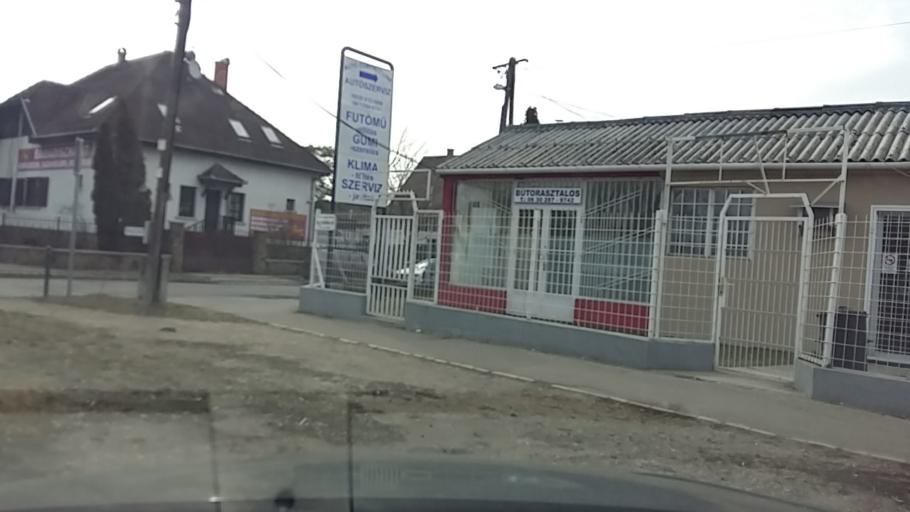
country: HU
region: Pest
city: Gyal
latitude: 47.4032
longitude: 19.1868
